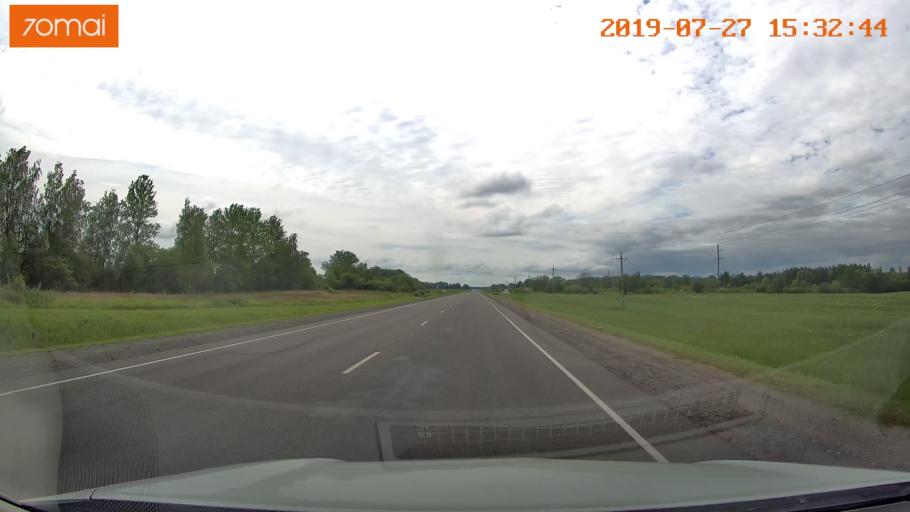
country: RU
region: Kaliningrad
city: Nesterov
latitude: 54.6154
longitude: 22.4664
